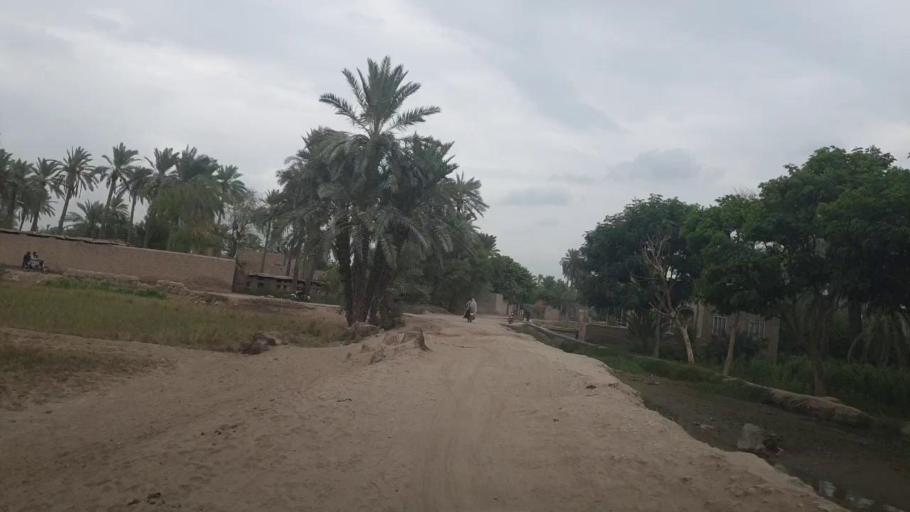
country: PK
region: Sindh
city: Khairpur
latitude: 27.5789
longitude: 68.7094
